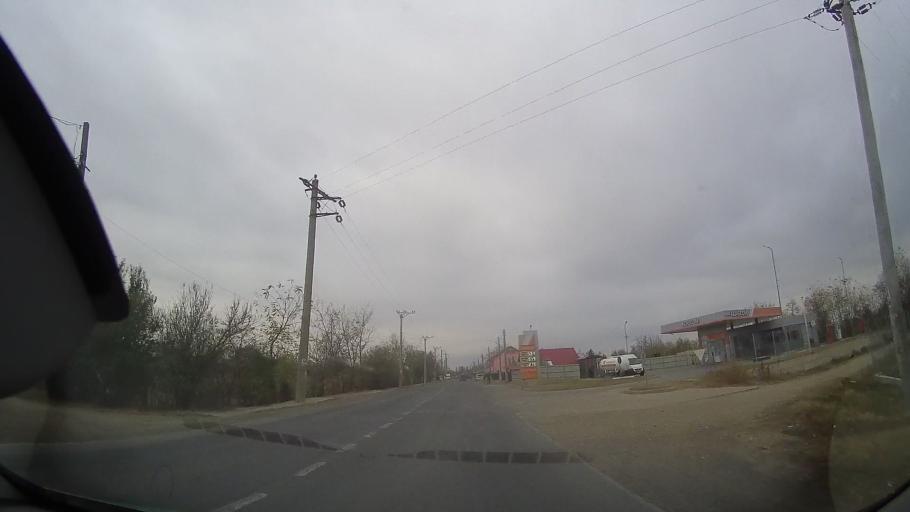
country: RO
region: Buzau
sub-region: Comuna Padina
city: Padina
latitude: 44.8214
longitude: 27.1174
